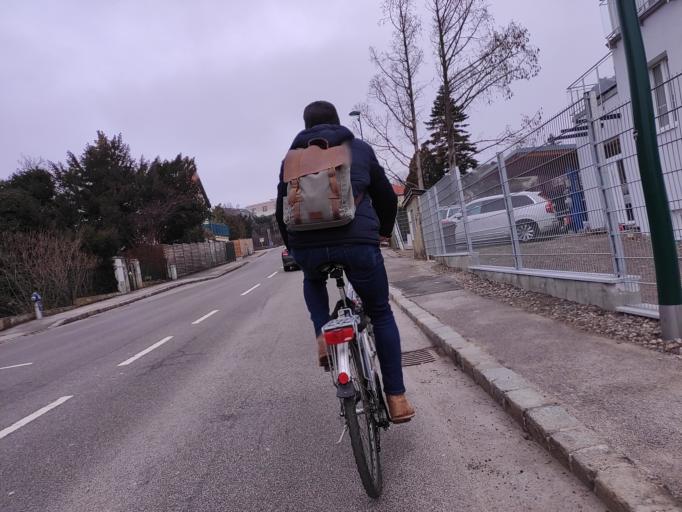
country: AT
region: Lower Austria
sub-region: Politischer Bezirk Modling
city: Hinterbruehl
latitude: 48.0939
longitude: 16.2605
